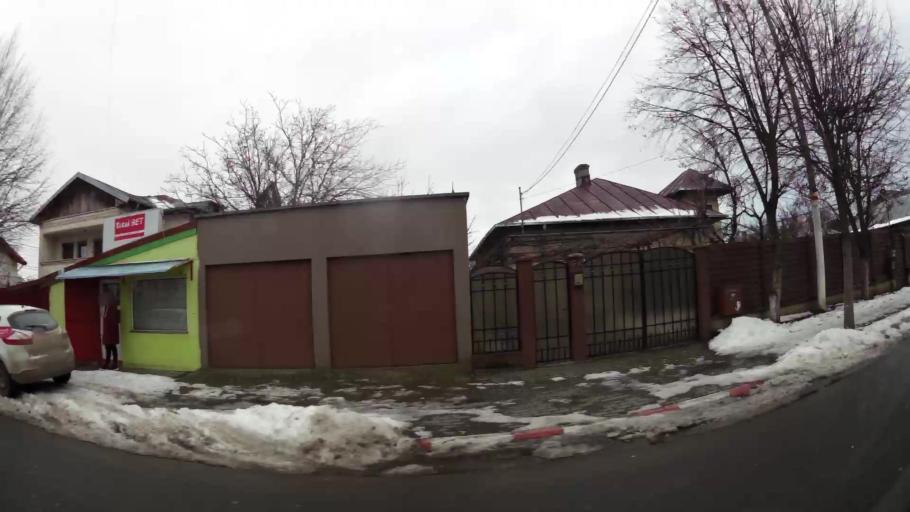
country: RO
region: Ilfov
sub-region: Voluntari City
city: Voluntari
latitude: 44.4988
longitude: 26.1962
